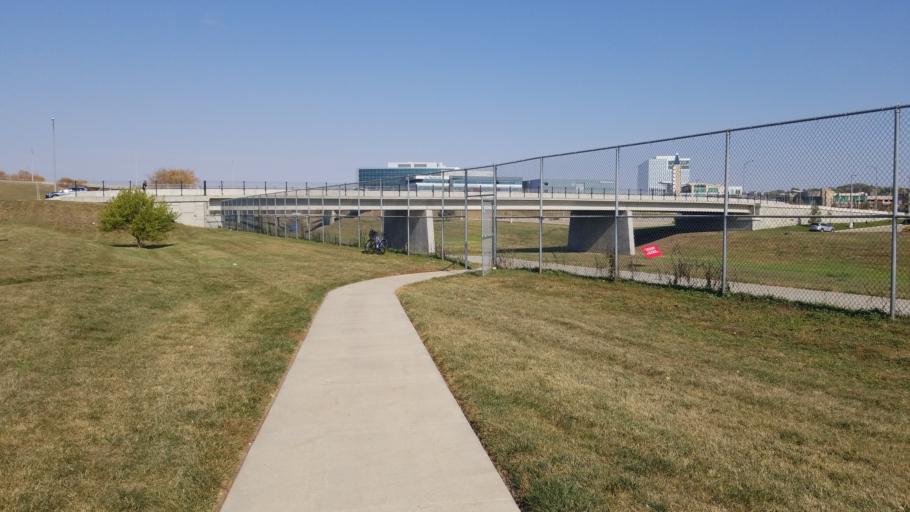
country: US
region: Nebraska
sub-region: Douglas County
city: Ralston
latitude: 41.2346
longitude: -96.0154
